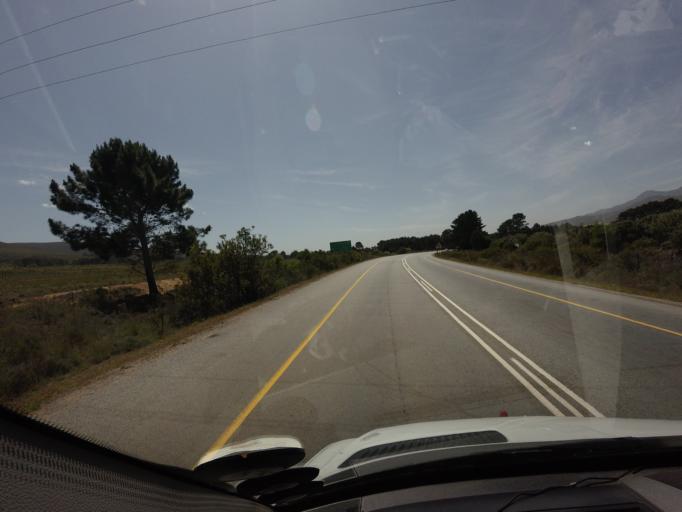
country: ZA
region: Western Cape
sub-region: Overberg District Municipality
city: Hermanus
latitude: -34.3005
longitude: 19.1392
